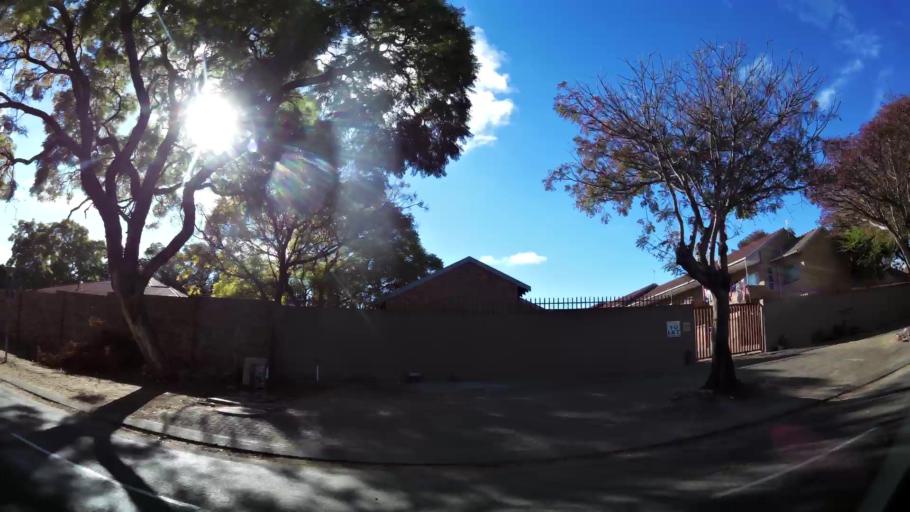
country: ZA
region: Limpopo
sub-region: Capricorn District Municipality
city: Polokwane
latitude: -23.9105
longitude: 29.4602
